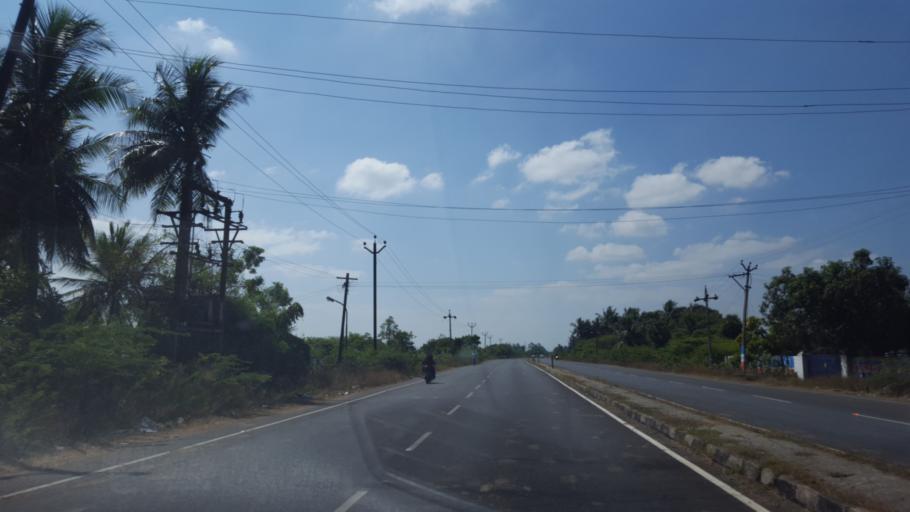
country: IN
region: Tamil Nadu
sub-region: Kancheepuram
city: Mamallapuram
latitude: 12.6898
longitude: 80.1800
